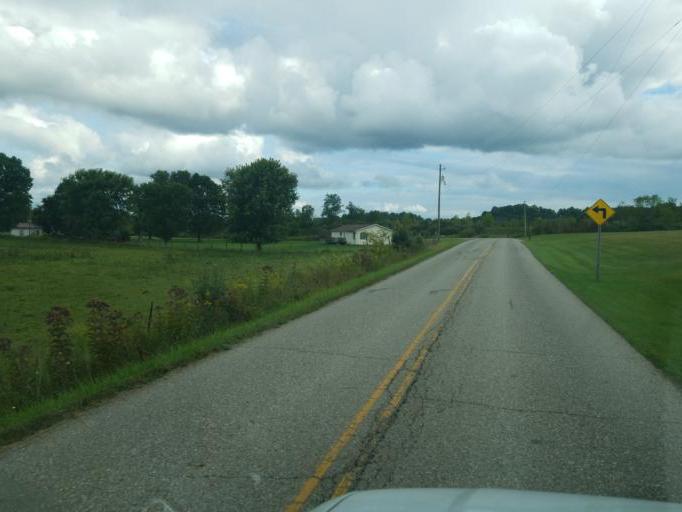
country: US
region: Ohio
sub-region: Jackson County
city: Oak Hill
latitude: 38.9373
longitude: -82.5774
